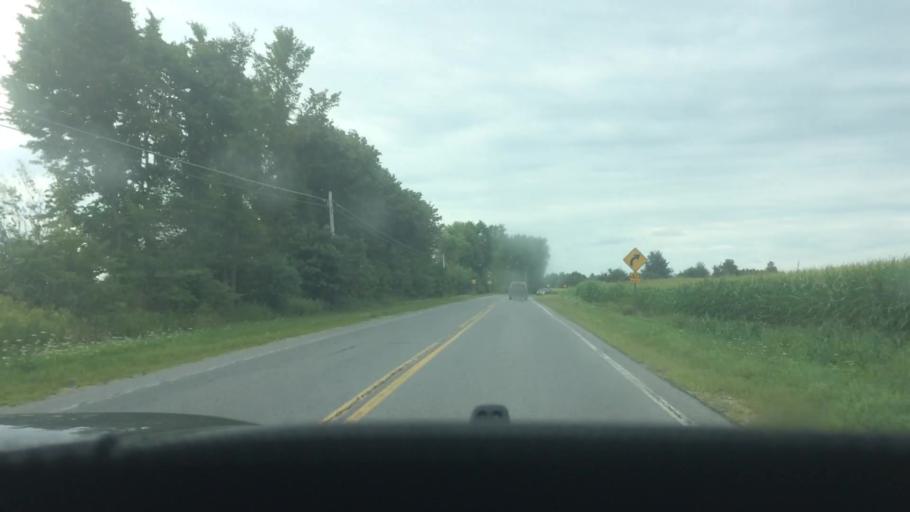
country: US
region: New York
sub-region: St. Lawrence County
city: Canton
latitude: 44.4924
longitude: -75.2166
